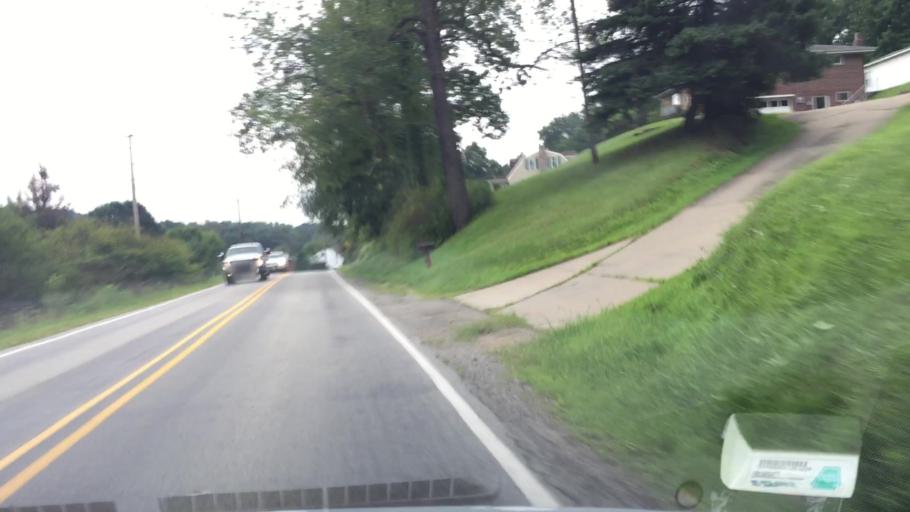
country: US
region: Pennsylvania
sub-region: Allegheny County
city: Curtisville
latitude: 40.6807
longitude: -79.8311
